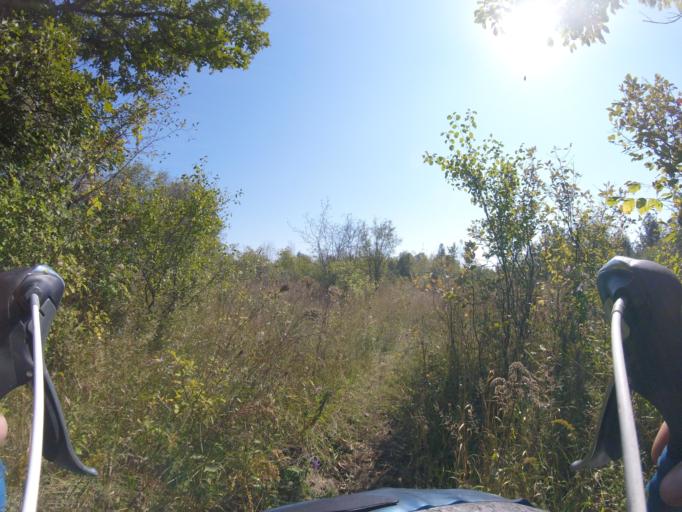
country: CA
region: Ontario
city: Bells Corners
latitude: 45.3159
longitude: -75.8580
